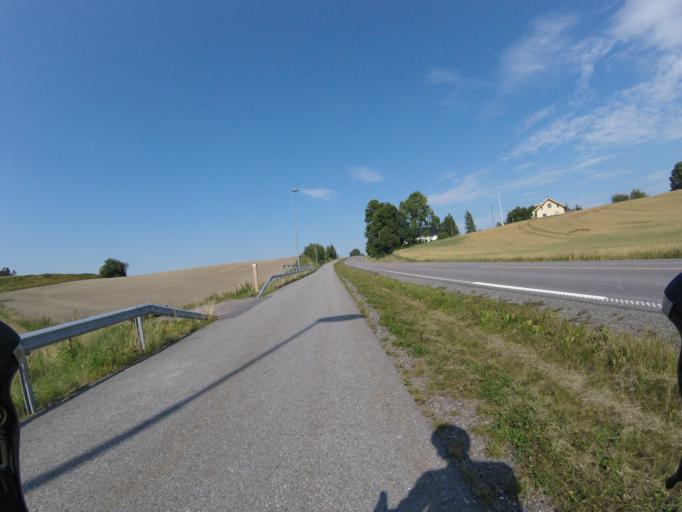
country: NO
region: Akershus
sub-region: Sorum
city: Frogner
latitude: 60.0177
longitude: 11.1118
